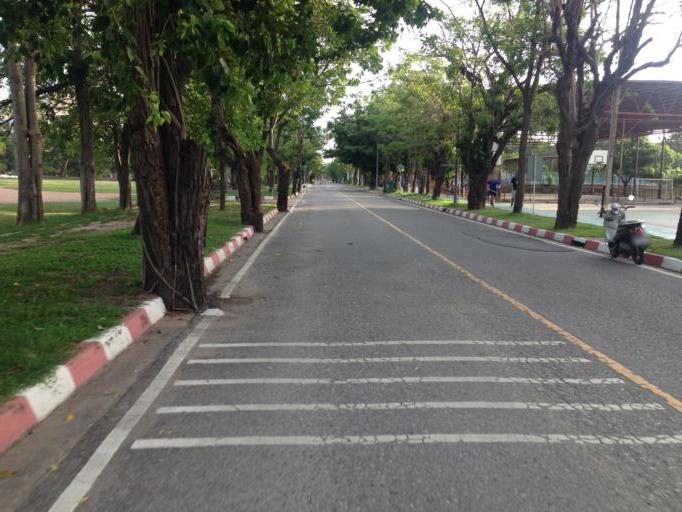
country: TH
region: Chon Buri
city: Si Racha
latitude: 13.2744
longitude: 100.9266
